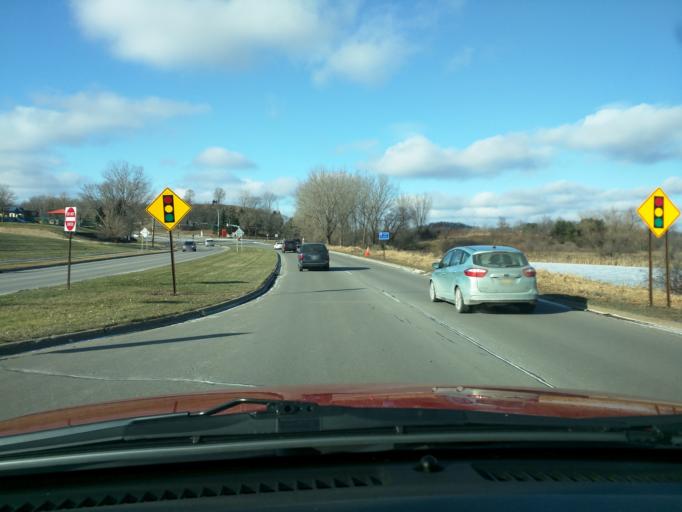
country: US
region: Minnesota
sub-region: Hennepin County
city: Eden Prairie
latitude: 44.8681
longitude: -93.4223
